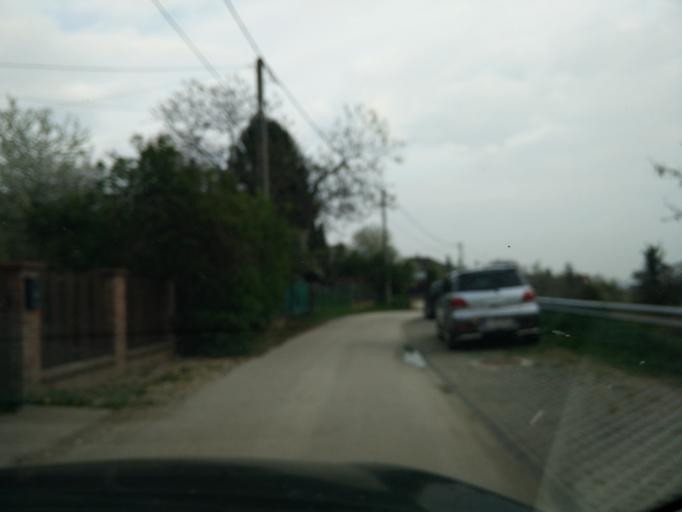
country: HU
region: Pest
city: Budaors
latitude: 47.4700
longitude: 18.9552
